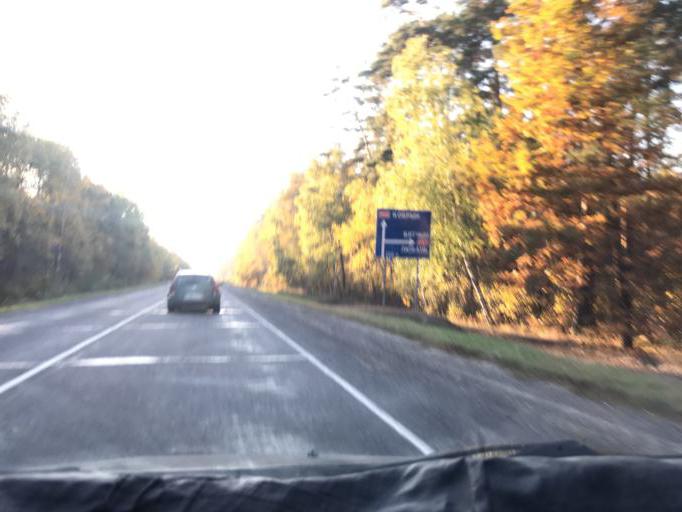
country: BY
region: Gomel
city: Zhytkavichy
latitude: 52.2680
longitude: 27.9632
